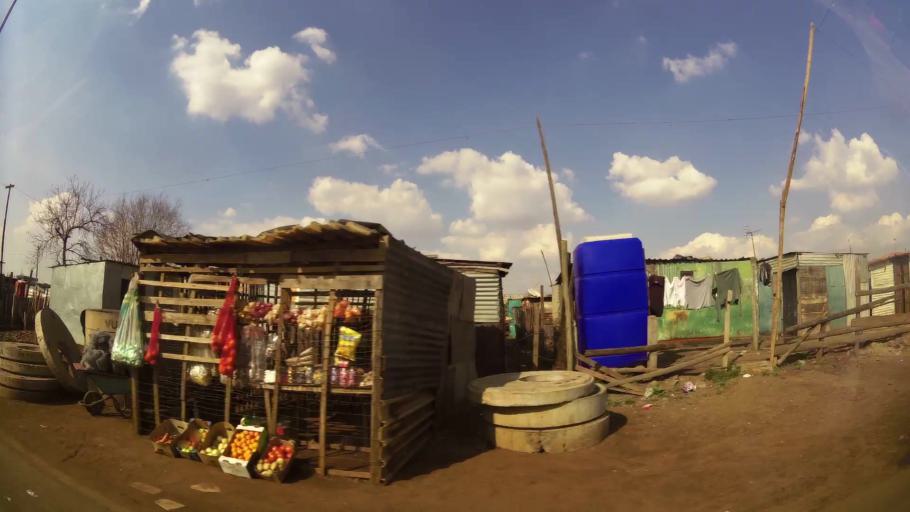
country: ZA
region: Gauteng
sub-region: Ekurhuleni Metropolitan Municipality
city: Germiston
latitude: -26.3331
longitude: 28.1399
